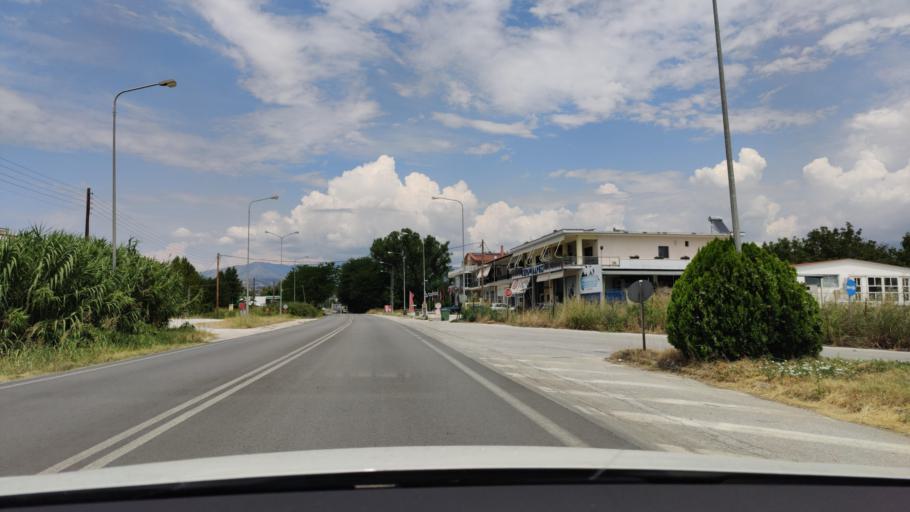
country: GR
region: Central Macedonia
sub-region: Nomos Serron
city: Serres
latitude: 41.0678
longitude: 23.5405
